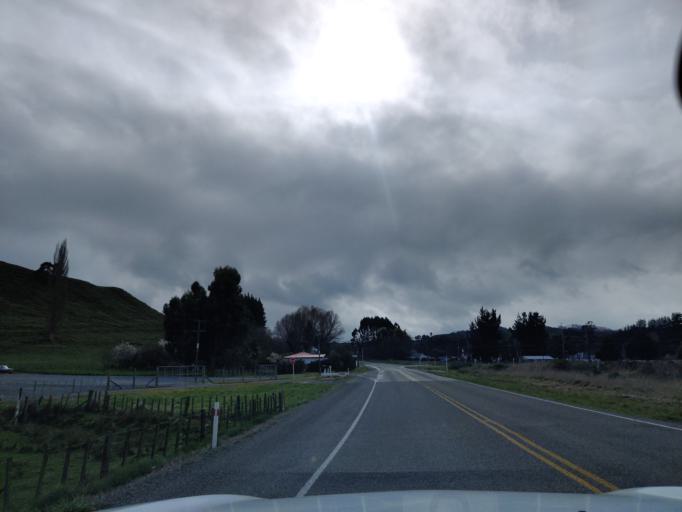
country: NZ
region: Manawatu-Wanganui
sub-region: Ruapehu District
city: Waiouru
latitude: -39.7349
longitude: 175.8427
